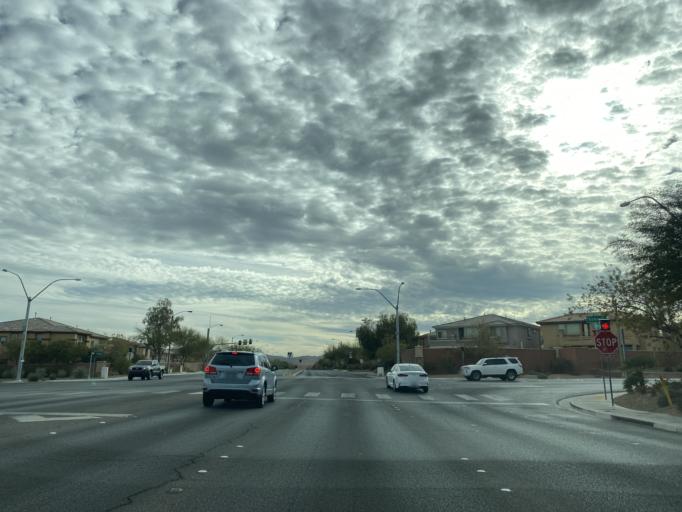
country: US
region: Nevada
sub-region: Clark County
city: Enterprise
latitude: 36.0127
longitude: -115.2800
